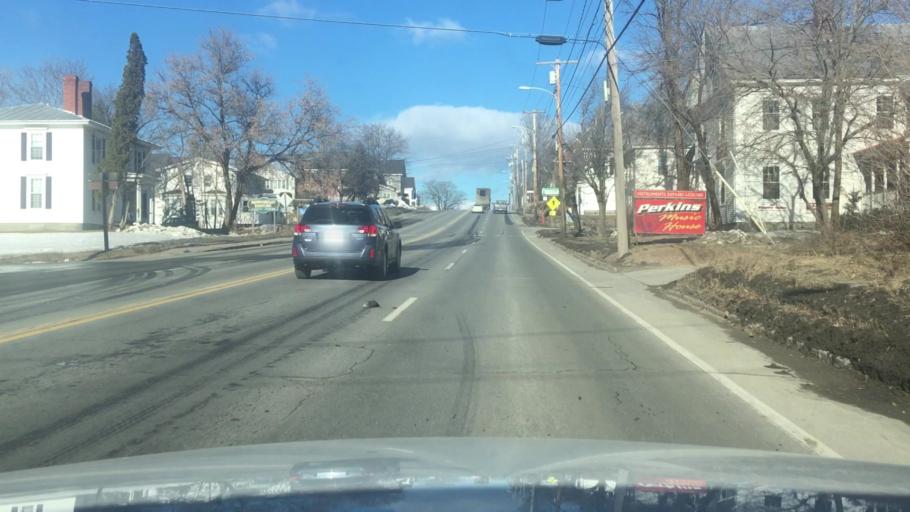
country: US
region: Maine
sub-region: Somerset County
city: Skowhegan
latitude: 44.7704
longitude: -69.7218
